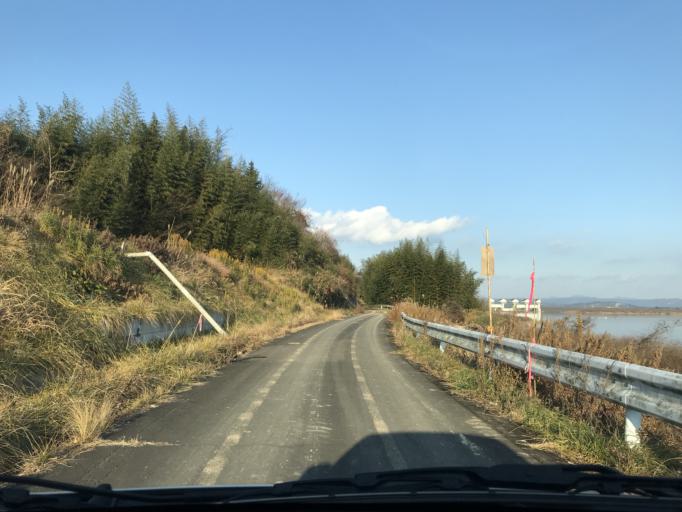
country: JP
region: Miyagi
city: Wakuya
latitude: 38.7045
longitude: 141.1369
